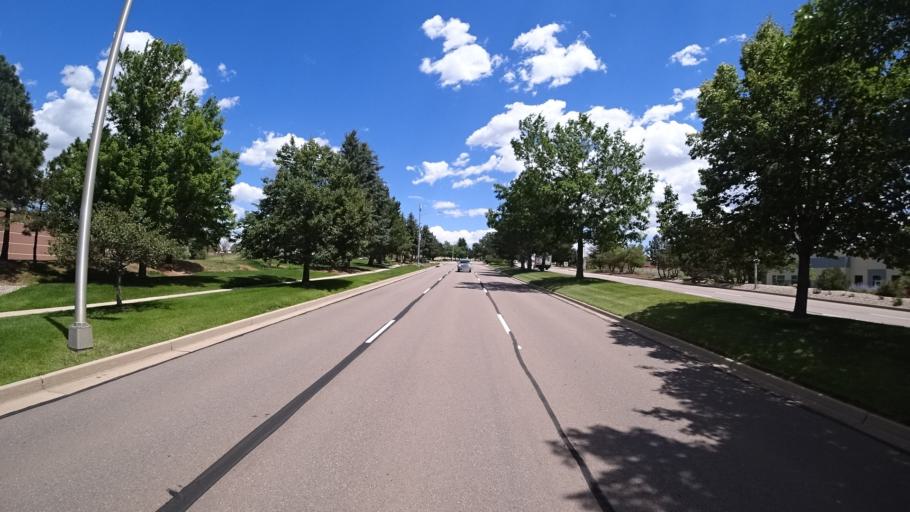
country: US
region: Colorado
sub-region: El Paso County
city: Air Force Academy
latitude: 38.9603
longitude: -104.7898
